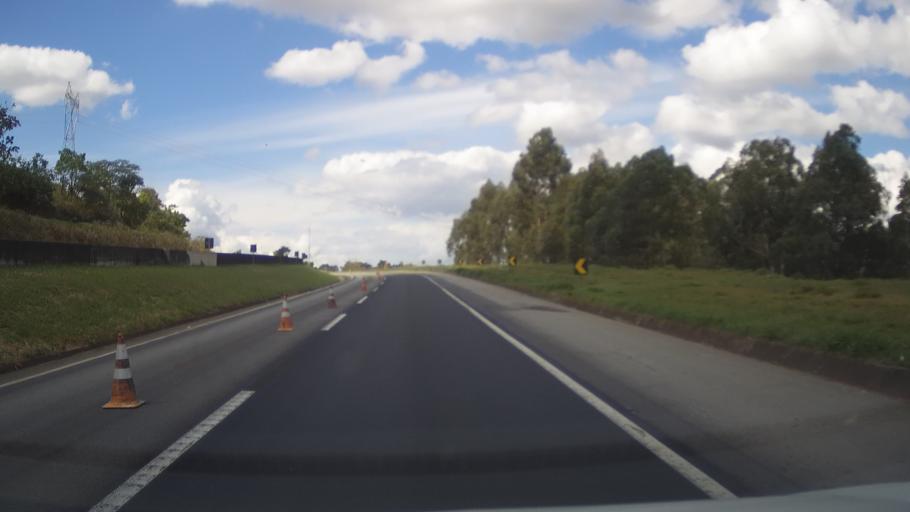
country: BR
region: Minas Gerais
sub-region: Santo Antonio Do Amparo
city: Santo Antonio do Amparo
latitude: -20.8401
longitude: -44.8251
